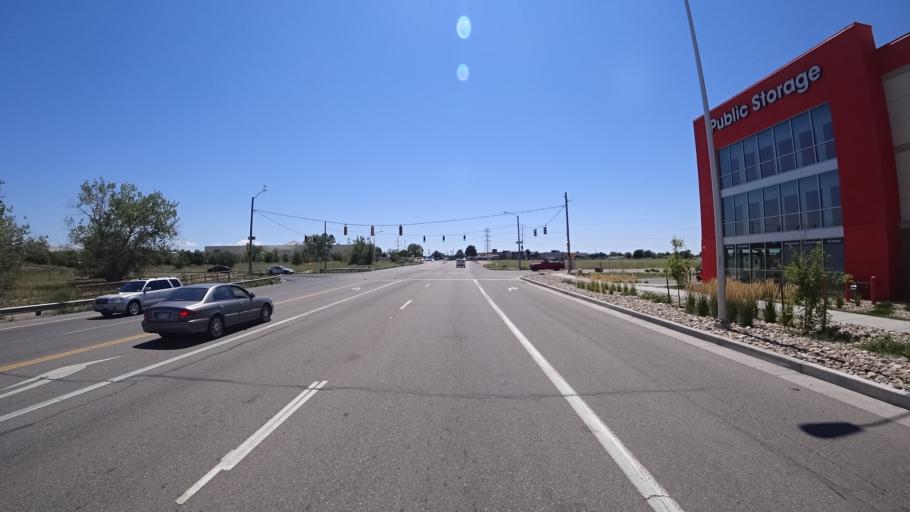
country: US
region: Colorado
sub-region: El Paso County
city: Stratmoor
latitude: 38.7910
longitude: -104.7633
